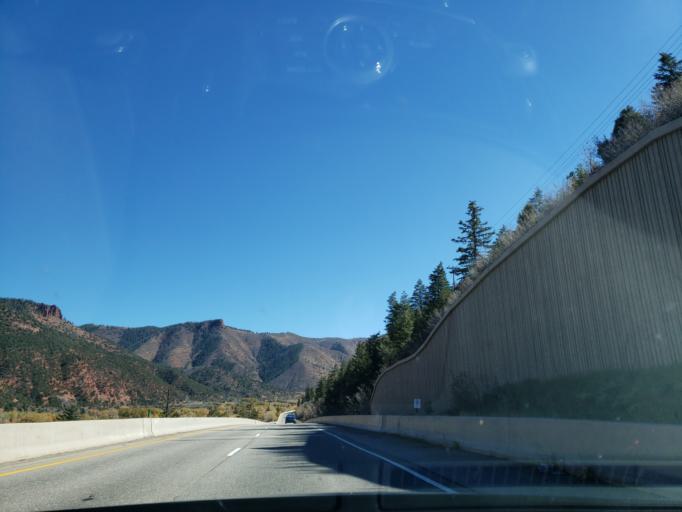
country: US
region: Colorado
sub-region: Eagle County
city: Basalt
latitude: 39.3286
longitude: -106.9666
